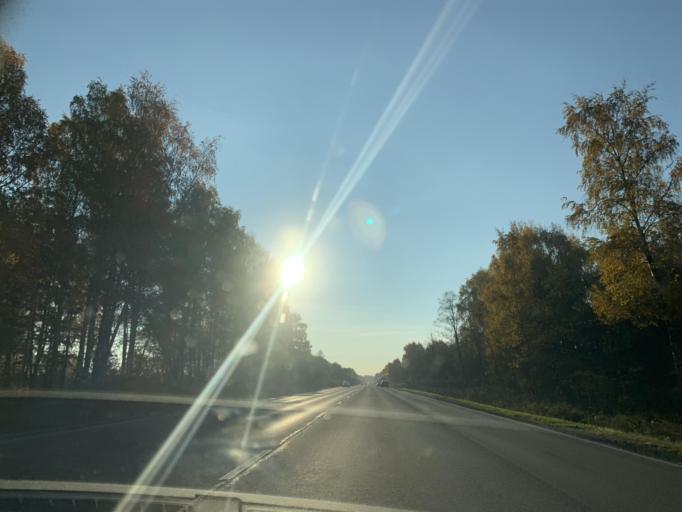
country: RU
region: Jaroslavl
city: Konstantinovskiy
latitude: 57.7493
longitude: 39.7060
